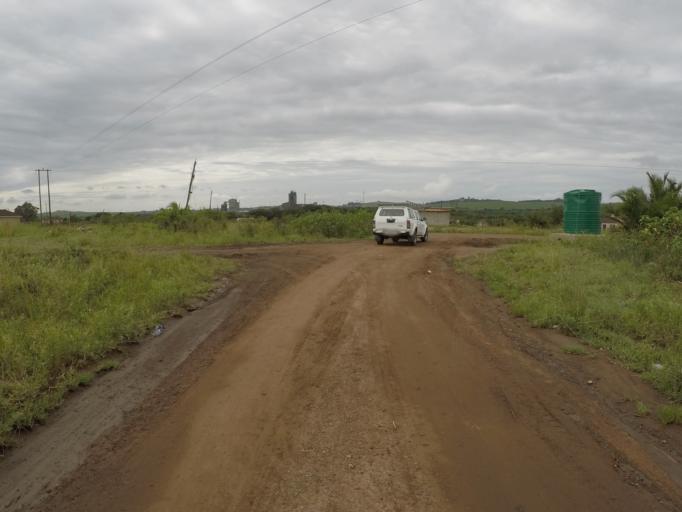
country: ZA
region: KwaZulu-Natal
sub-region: uThungulu District Municipality
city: Empangeni
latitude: -28.7127
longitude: 31.8628
